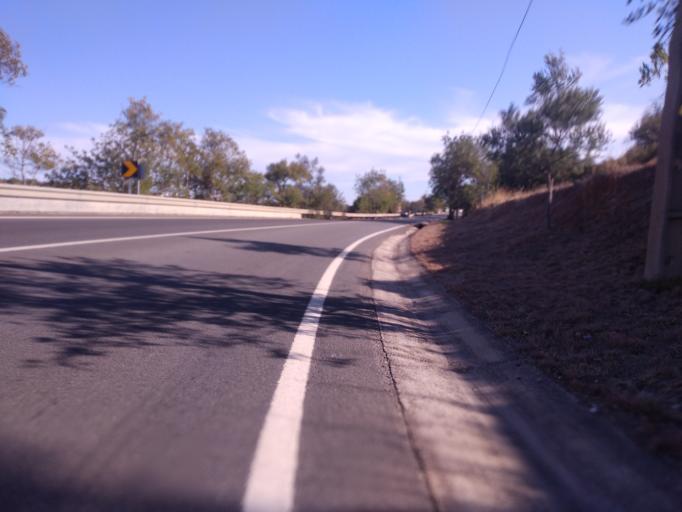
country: PT
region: Faro
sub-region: Sao Bras de Alportel
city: Sao Bras de Alportel
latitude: 37.1036
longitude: -7.9046
